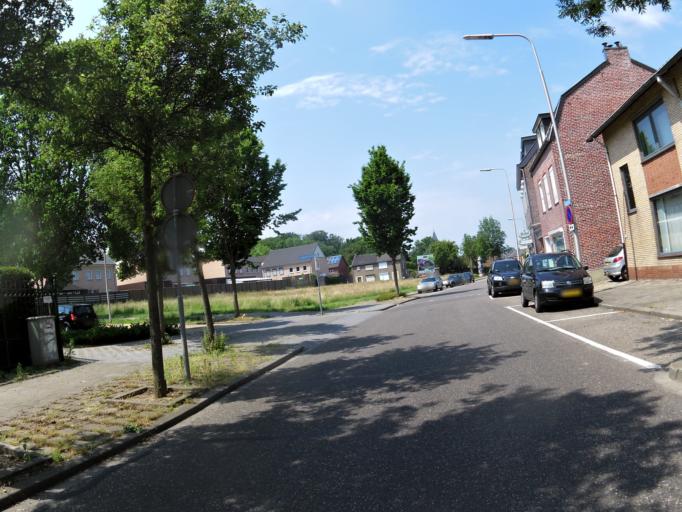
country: DE
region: North Rhine-Westphalia
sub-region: Regierungsbezirk Koln
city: Herzogenrath
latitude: 50.8790
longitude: 6.0809
